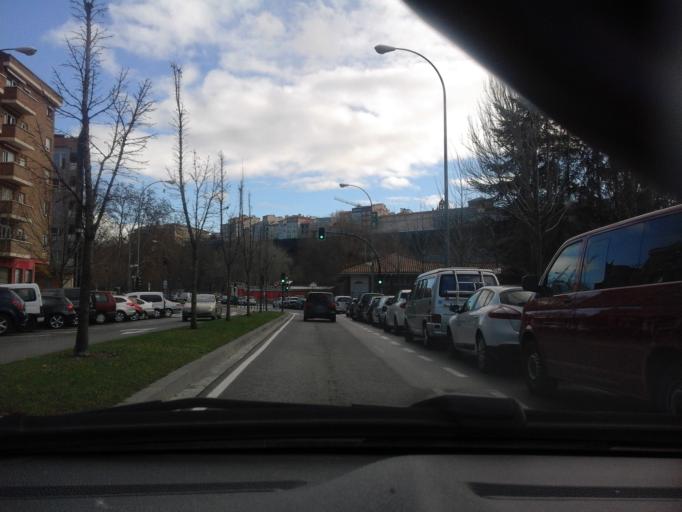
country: ES
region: Navarre
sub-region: Provincia de Navarra
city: Primer Ensanche
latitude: 42.8211
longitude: -1.6522
